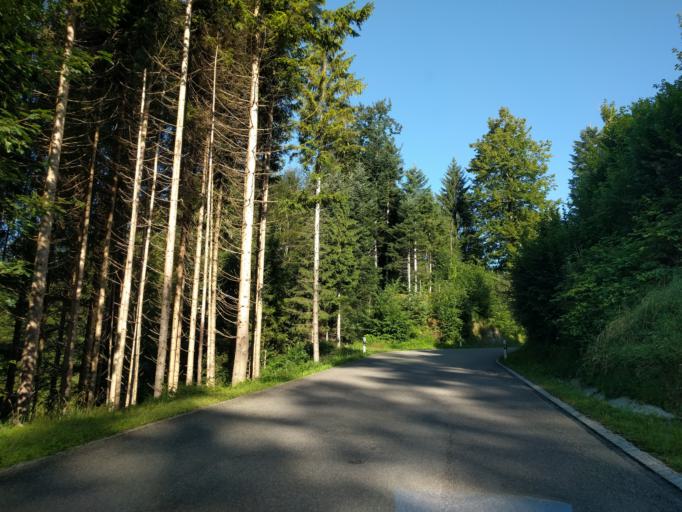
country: CH
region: Saint Gallen
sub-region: Wahlkreis Toggenburg
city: Sankt Peterzell
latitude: 47.2990
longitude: 9.1904
